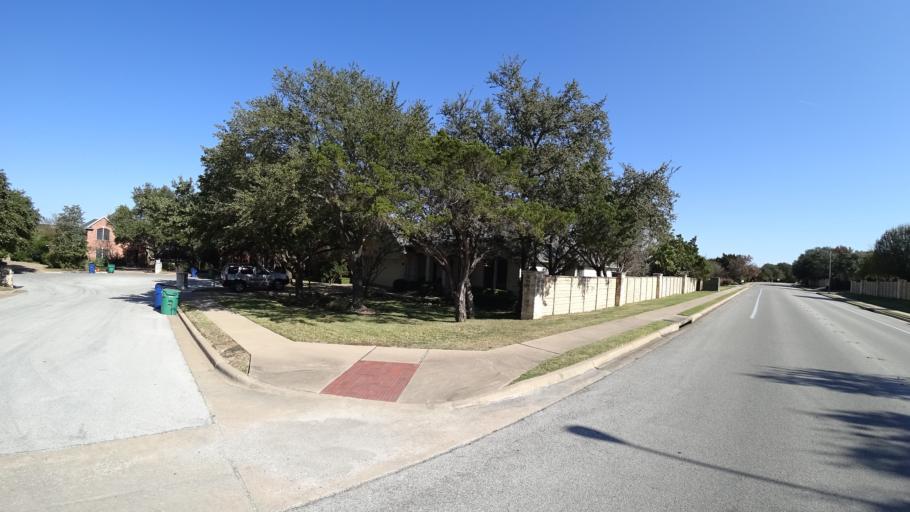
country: US
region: Texas
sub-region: Travis County
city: Lost Creek
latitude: 30.3766
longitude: -97.8493
